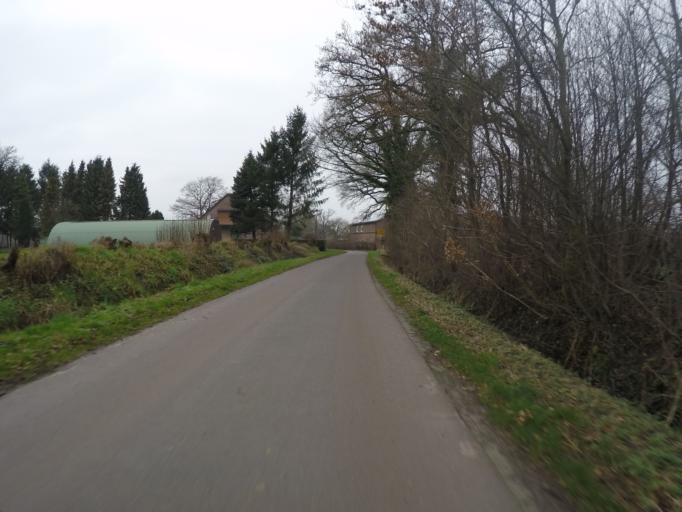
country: DE
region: Schleswig-Holstein
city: Borstel-Hohenraden
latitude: 53.6828
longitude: 9.8177
